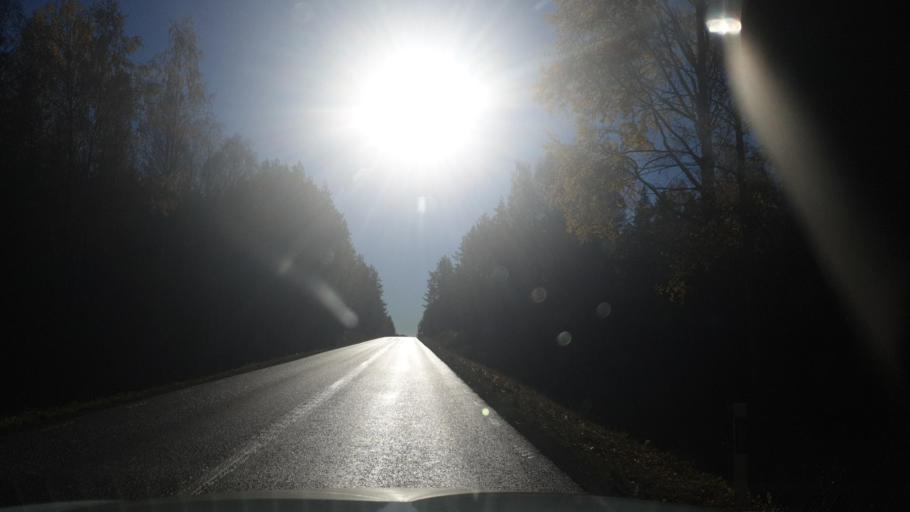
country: SE
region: Vaermland
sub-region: Arvika Kommun
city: Arvika
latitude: 59.5710
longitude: 12.7151
